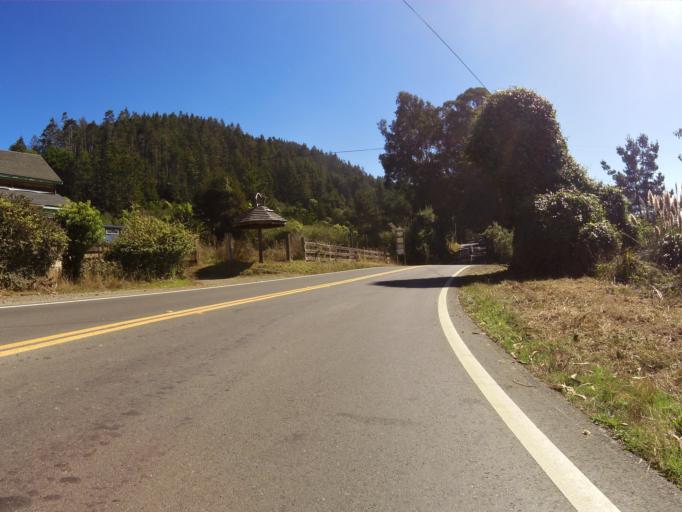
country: US
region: California
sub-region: Mendocino County
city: Fort Bragg
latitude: 39.6355
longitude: -123.7829
